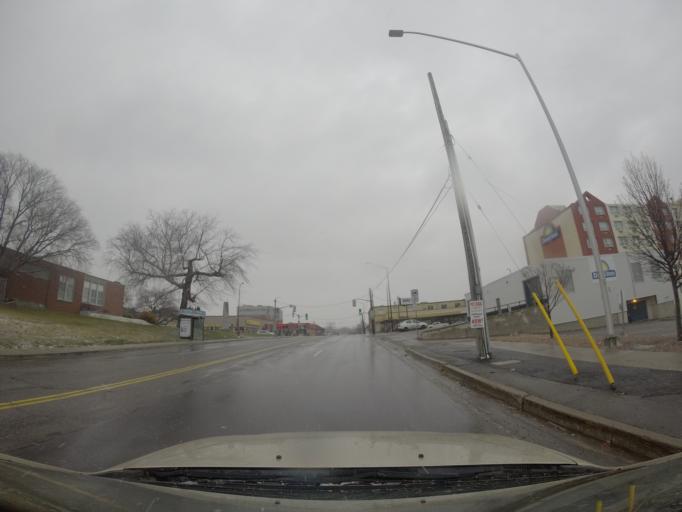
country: CA
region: Ontario
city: Greater Sudbury
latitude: 46.4924
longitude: -81.0005
